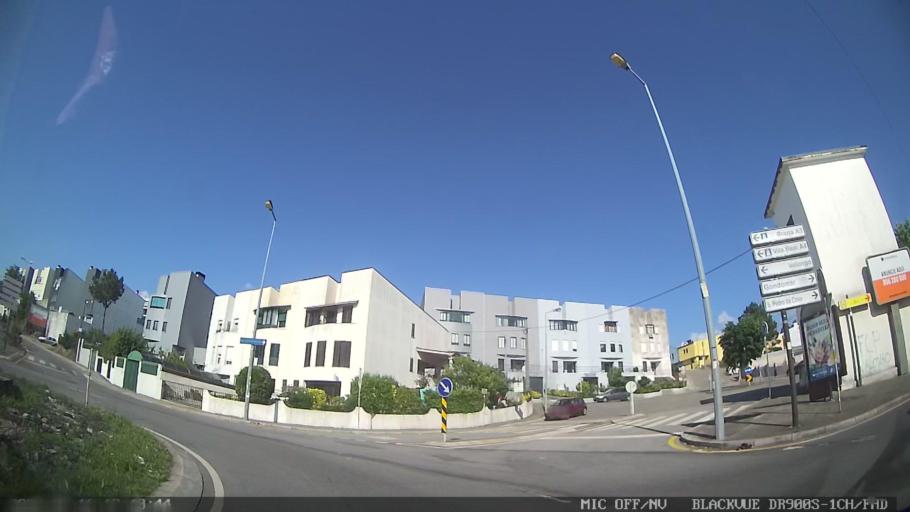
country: PT
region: Porto
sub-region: Valongo
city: Valongo
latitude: 41.1910
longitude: -8.5185
